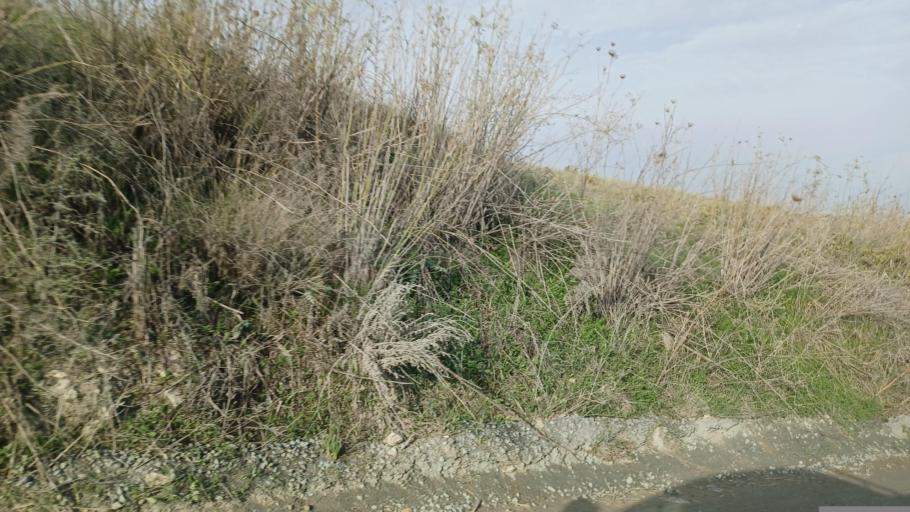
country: CY
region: Pafos
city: Tala
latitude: 34.9088
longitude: 32.4687
